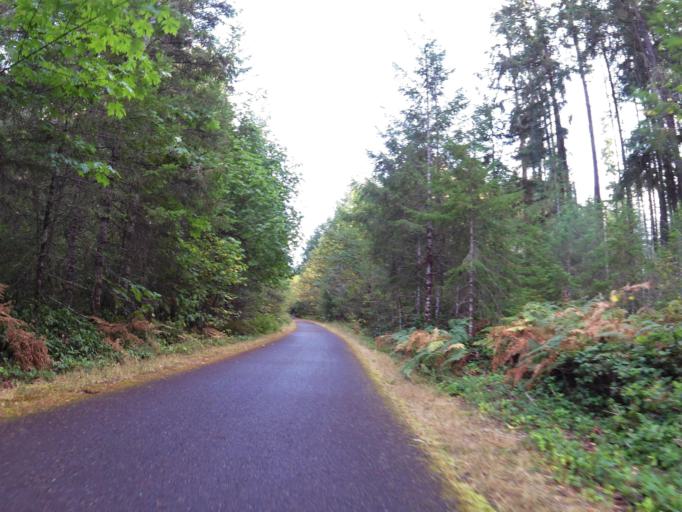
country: US
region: Washington
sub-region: Thurston County
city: Tenino
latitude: 46.9234
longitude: -122.8084
